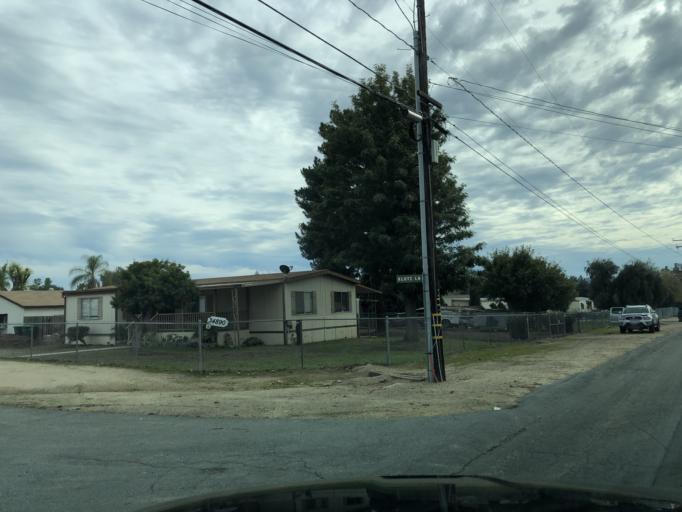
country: US
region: California
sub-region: Riverside County
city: Wildomar
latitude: 33.6142
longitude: -117.2712
